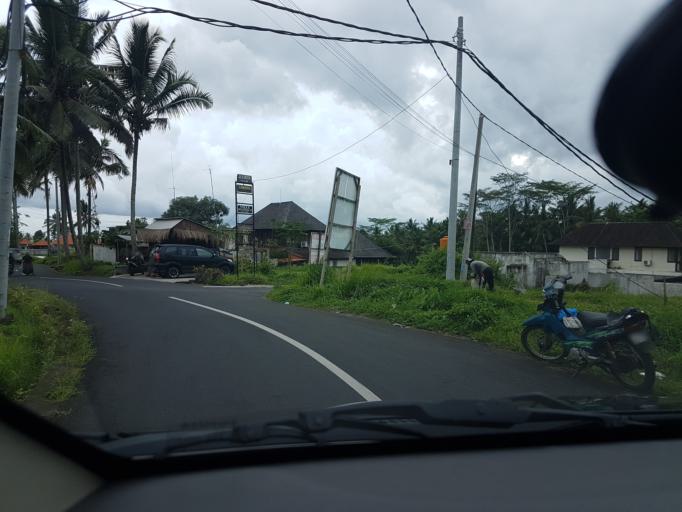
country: ID
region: Bali
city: Banjar Triwangsakeliki
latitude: -8.4645
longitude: 115.2731
